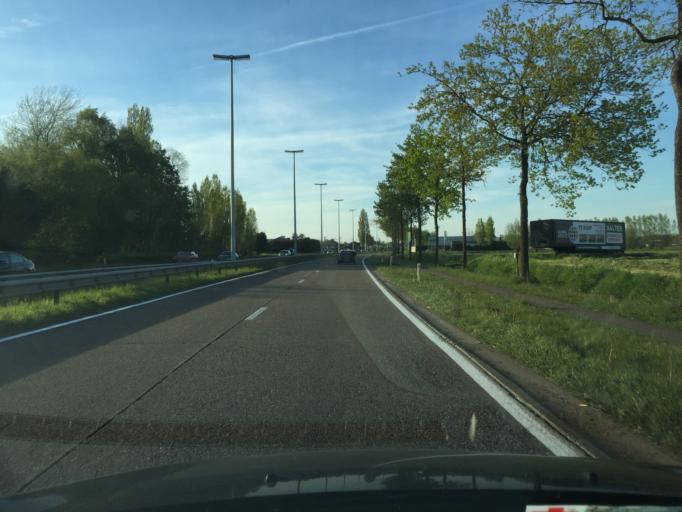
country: BE
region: Flanders
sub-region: Provincie Oost-Vlaanderen
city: Knesselare
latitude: 51.1267
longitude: 3.4239
